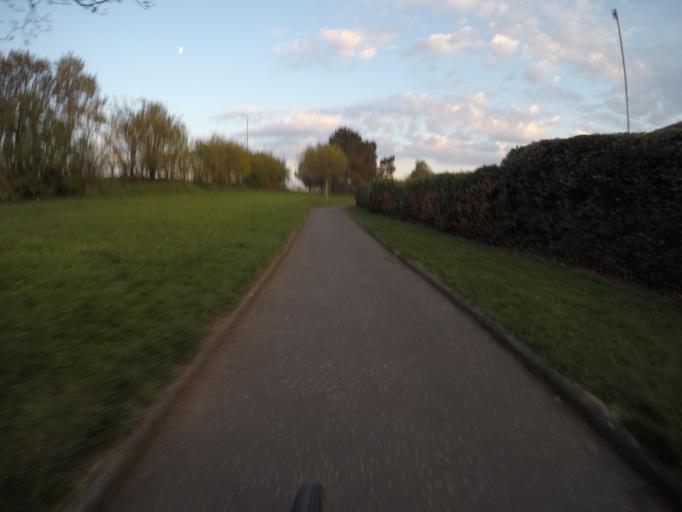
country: GB
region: Scotland
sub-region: South Ayrshire
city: Troon
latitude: 55.5661
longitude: -4.6389
